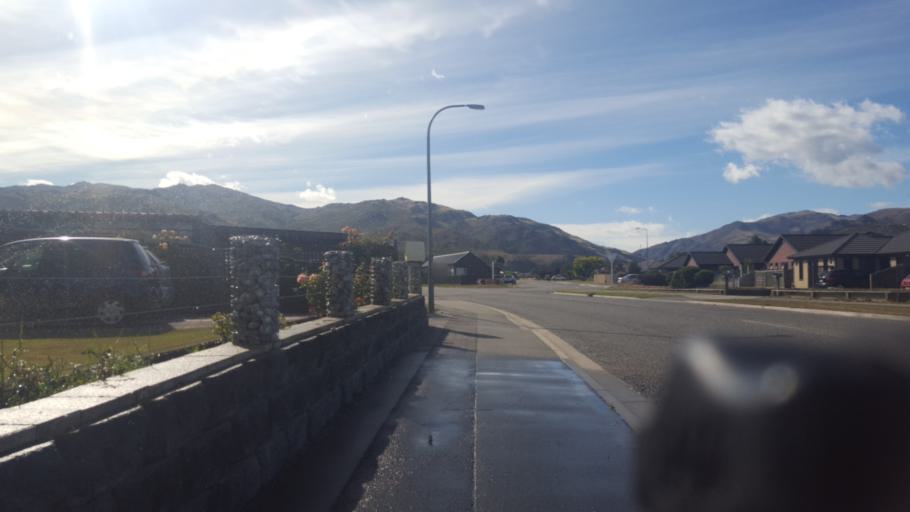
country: NZ
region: Otago
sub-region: Queenstown-Lakes District
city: Wanaka
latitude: -45.0460
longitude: 169.1959
